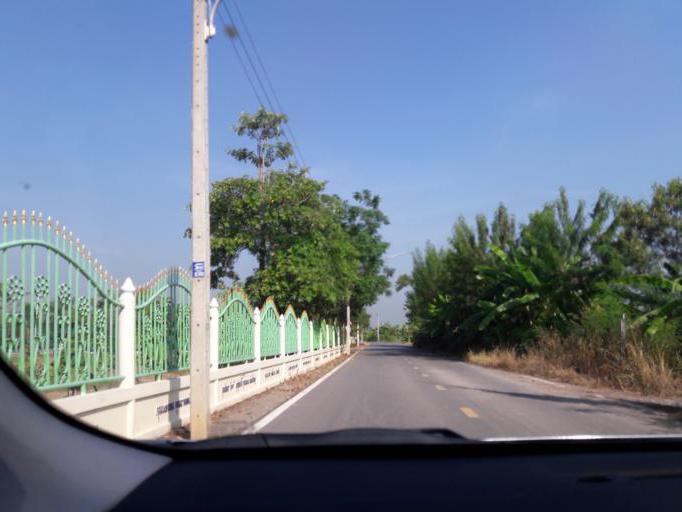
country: TH
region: Ang Thong
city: Ang Thong
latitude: 14.5896
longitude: 100.4308
